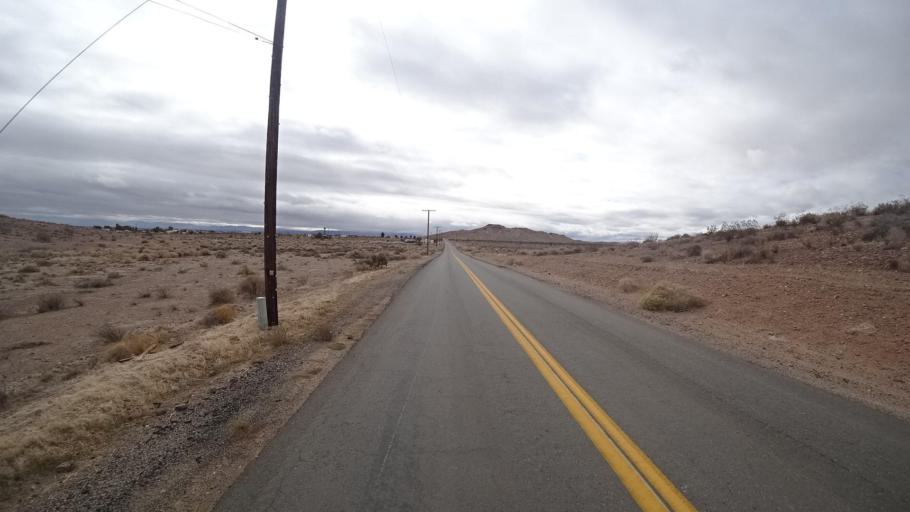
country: US
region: California
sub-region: Kern County
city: Rosamond
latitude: 34.8998
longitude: -118.2170
